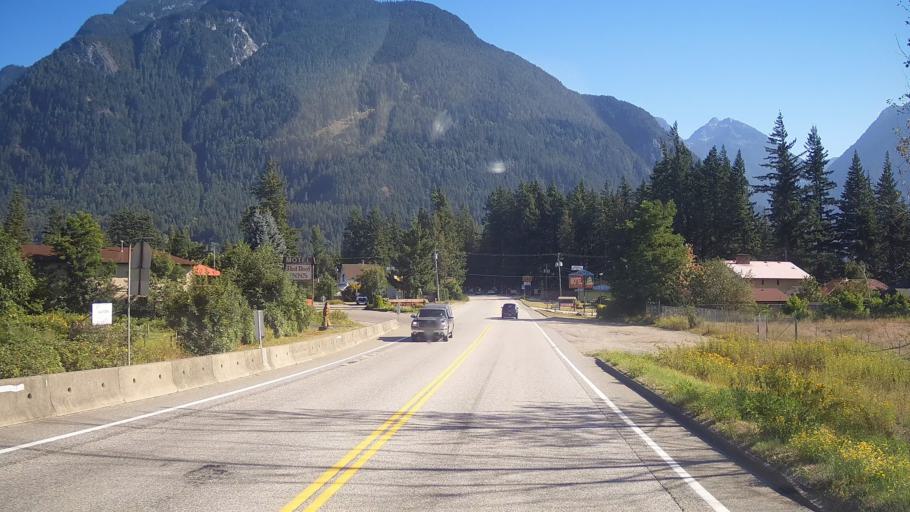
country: CA
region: British Columbia
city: Hope
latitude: 49.3851
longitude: -121.4480
